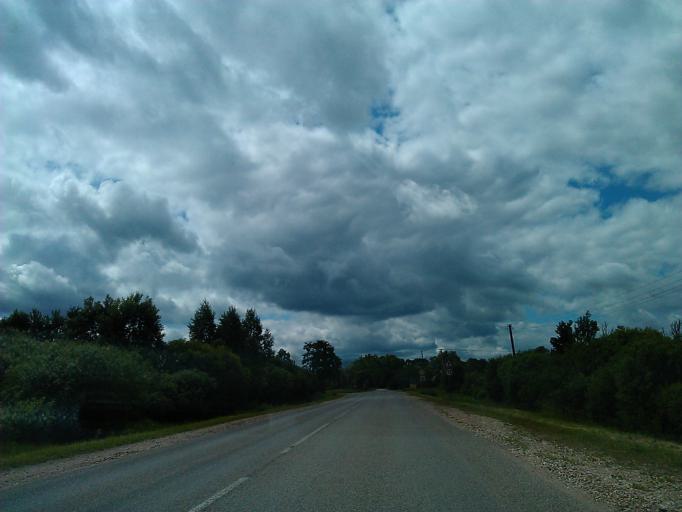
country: LV
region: Talsu Rajons
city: Stende
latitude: 57.0789
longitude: 22.2936
